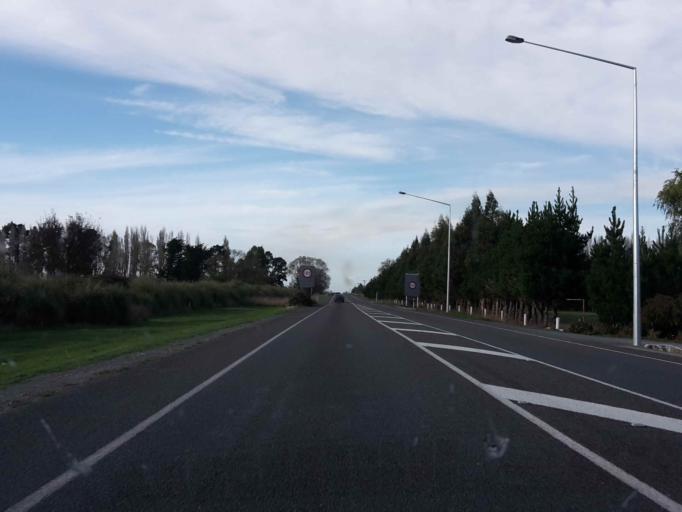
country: NZ
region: Canterbury
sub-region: Ashburton District
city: Tinwald
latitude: -43.9979
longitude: 171.5767
